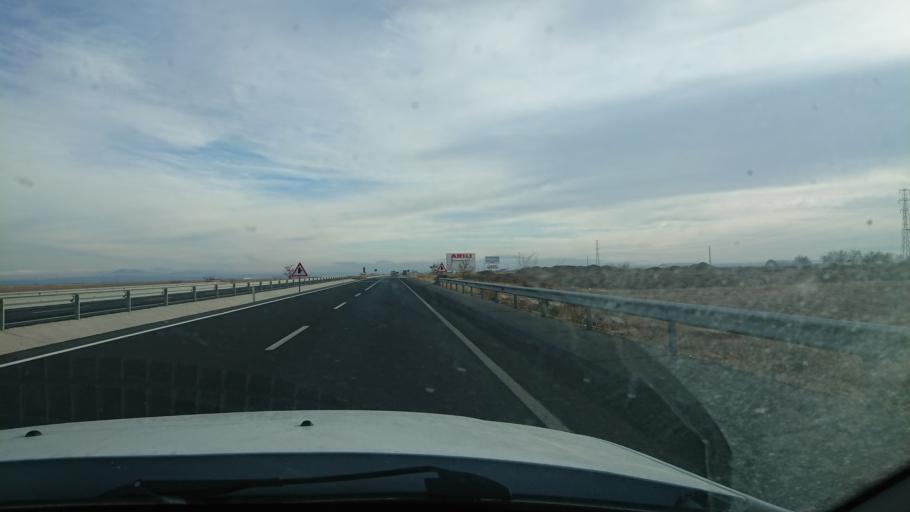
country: TR
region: Aksaray
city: Yesilova
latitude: 38.2969
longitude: 33.7842
